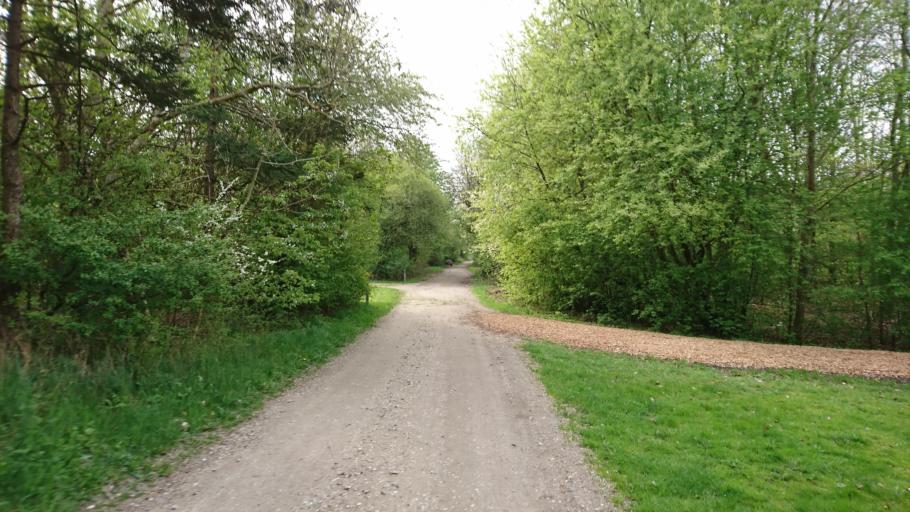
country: DK
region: Capital Region
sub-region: Ballerup Kommune
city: Ballerup
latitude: 55.7445
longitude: 12.3992
